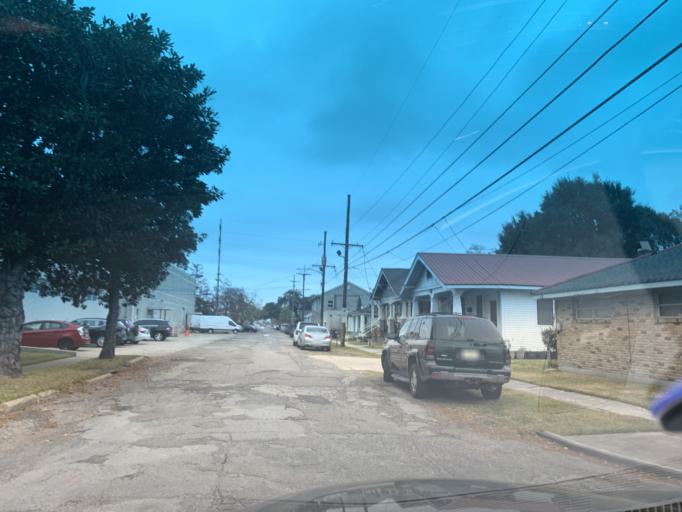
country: US
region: Louisiana
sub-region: Orleans Parish
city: New Orleans
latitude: 29.9826
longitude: -90.1066
